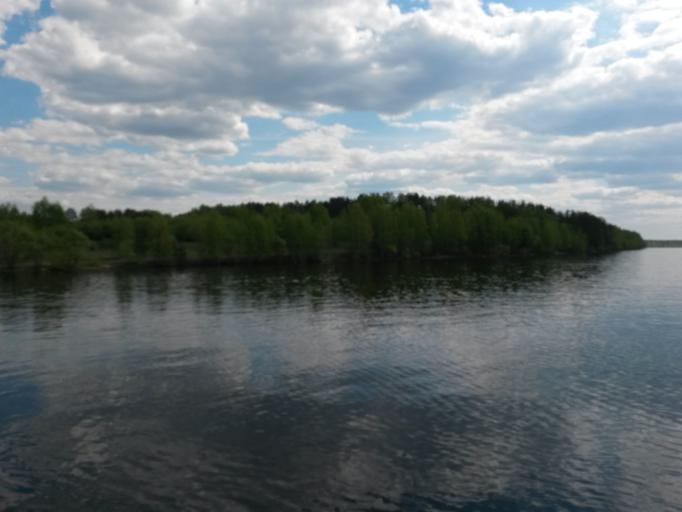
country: RU
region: Jaroslavl
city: Myshkin
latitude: 57.7763
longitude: 38.4582
